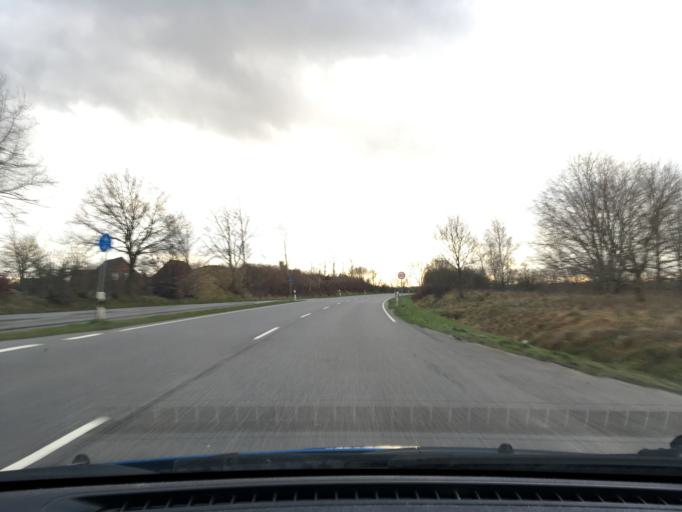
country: DE
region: Schleswig-Holstein
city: Ottenbuttel
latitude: 53.9805
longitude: 9.5001
